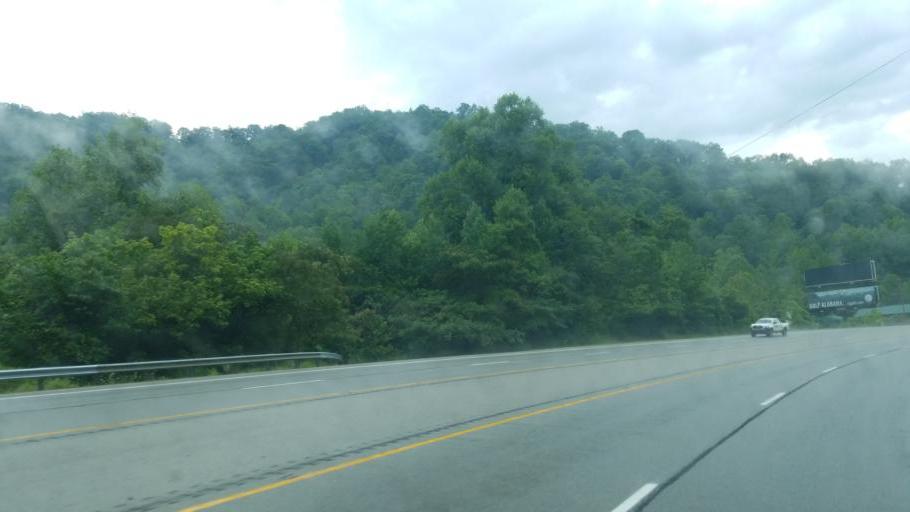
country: US
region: West Virginia
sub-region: Mingo County
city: Williamson
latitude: 37.6433
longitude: -82.2621
